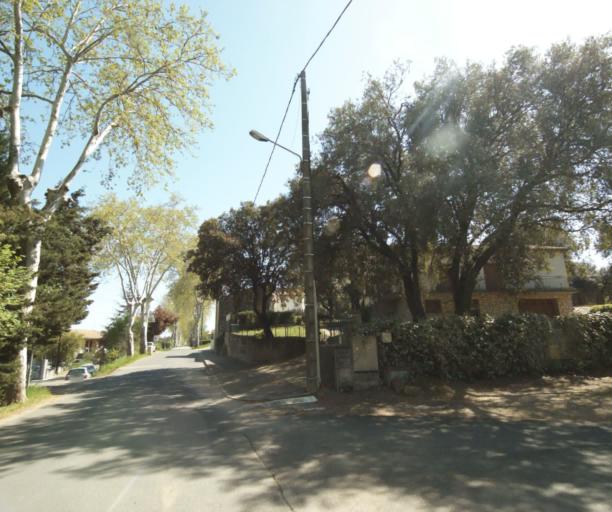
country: FR
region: Languedoc-Roussillon
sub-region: Departement de l'Herault
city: Saint-Drezery
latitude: 43.7307
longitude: 3.9819
